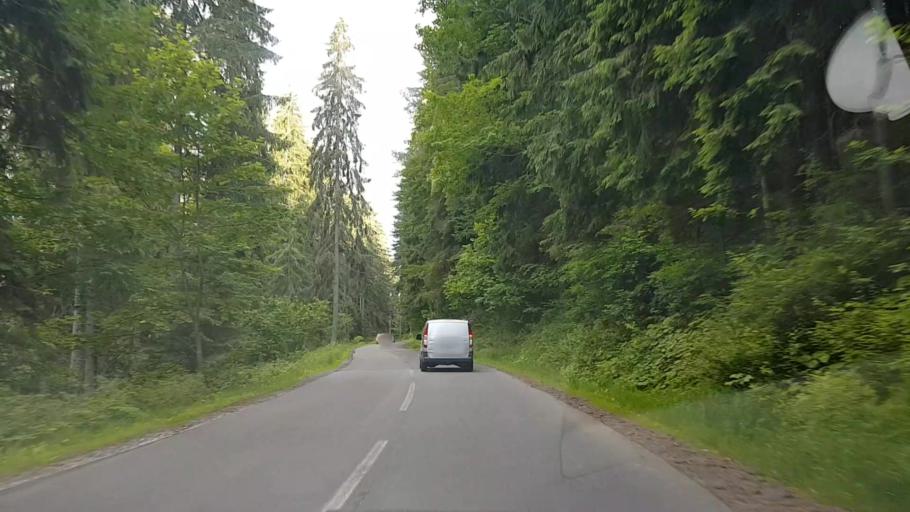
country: RO
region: Harghita
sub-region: Comuna Remetea
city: Remetea
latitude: 46.6730
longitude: 25.3403
